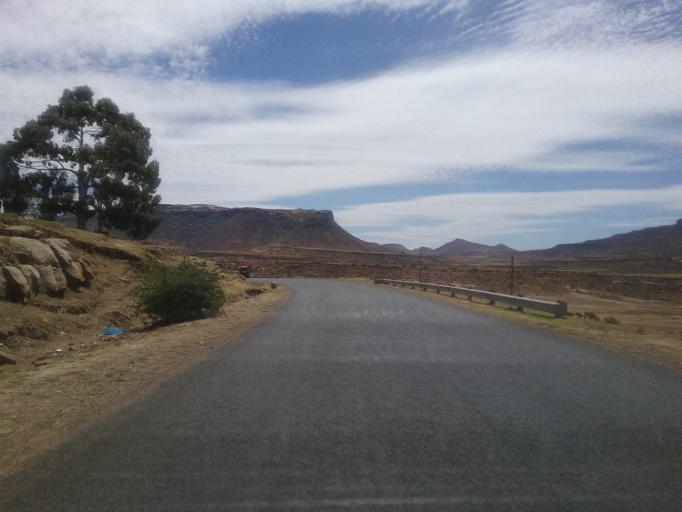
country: LS
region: Mafeteng
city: Mafeteng
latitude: -29.9071
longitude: 27.2508
